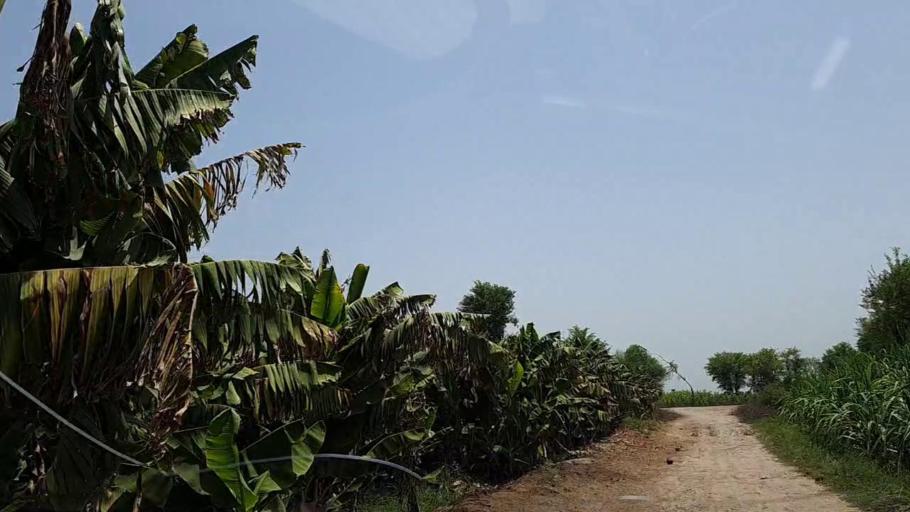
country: PK
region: Sindh
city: Tharu Shah
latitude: 26.9319
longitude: 68.0401
